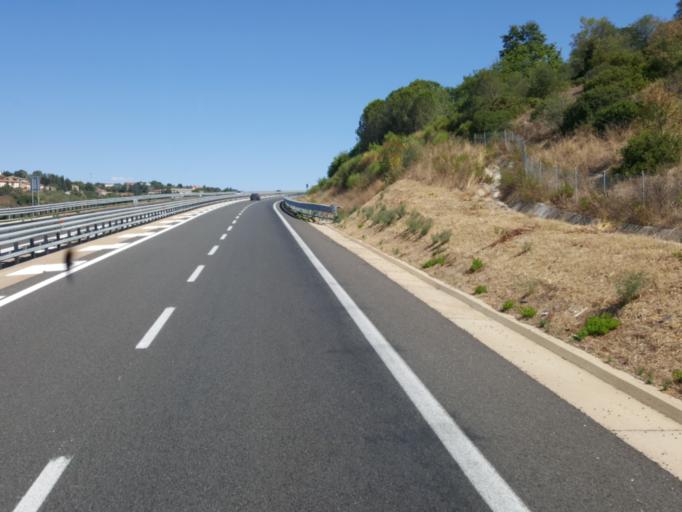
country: IT
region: Tuscany
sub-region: Provincia di Grosseto
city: Civitella Marittima
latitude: 42.9862
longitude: 11.2863
